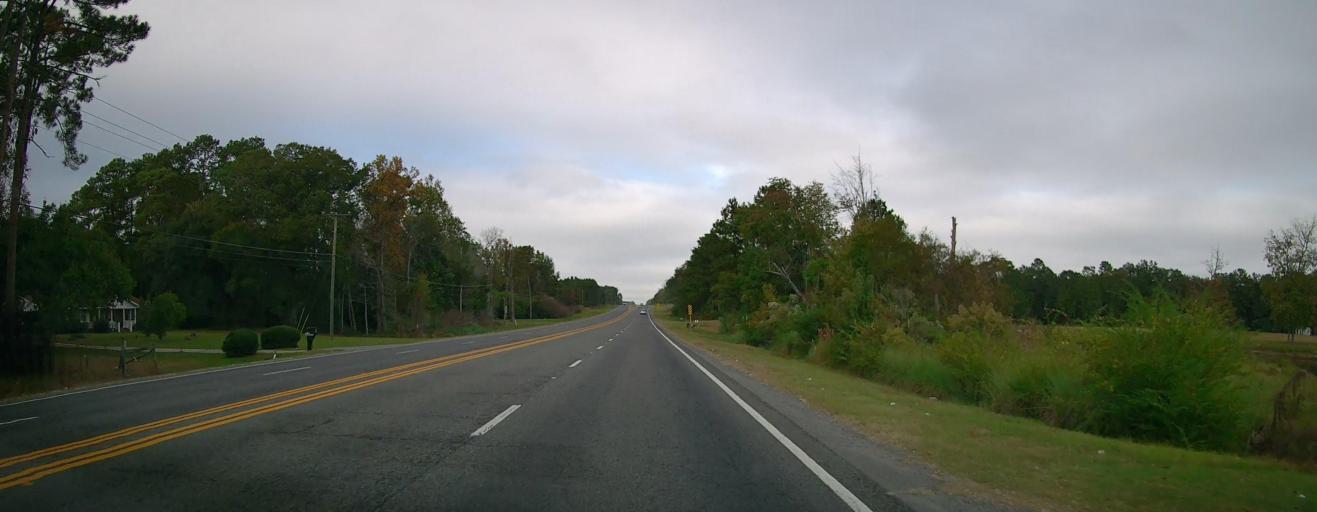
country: US
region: Georgia
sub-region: Tift County
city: Unionville
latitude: 31.4070
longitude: -83.5358
